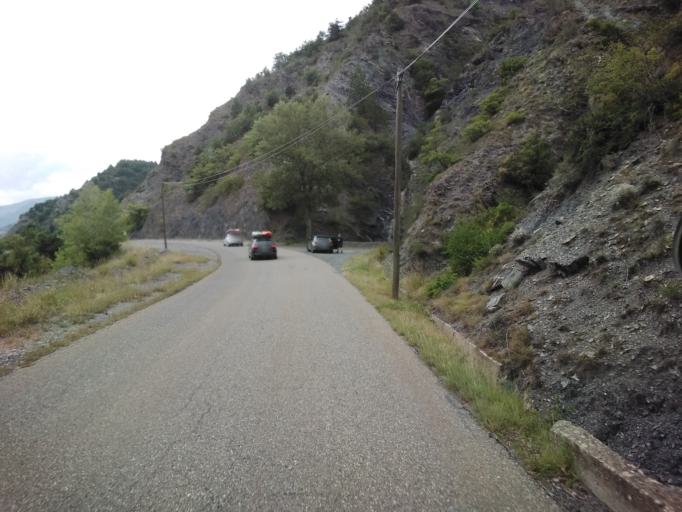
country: FR
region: Provence-Alpes-Cote d'Azur
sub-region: Departement des Alpes-de-Haute-Provence
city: Seyne-les-Alpes
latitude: 44.4614
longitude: 6.3726
